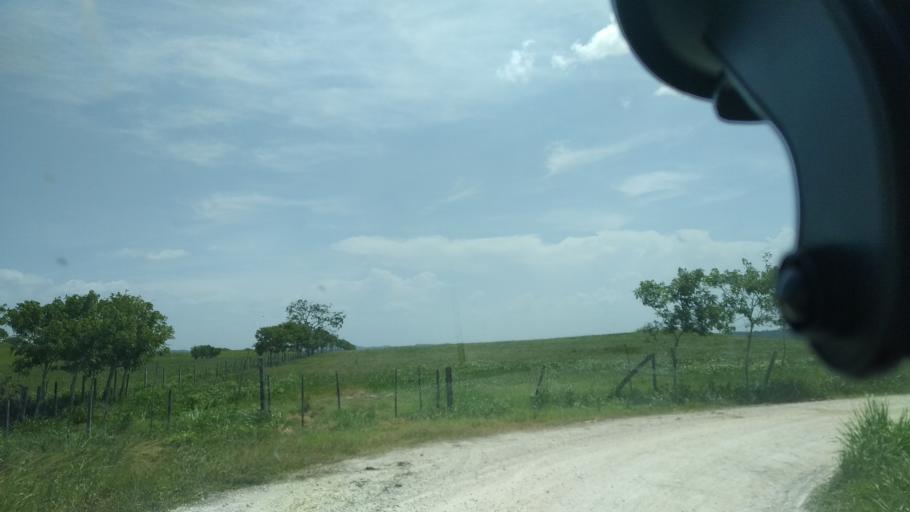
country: BZ
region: Cayo
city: San Ignacio
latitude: 17.2906
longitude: -89.0674
